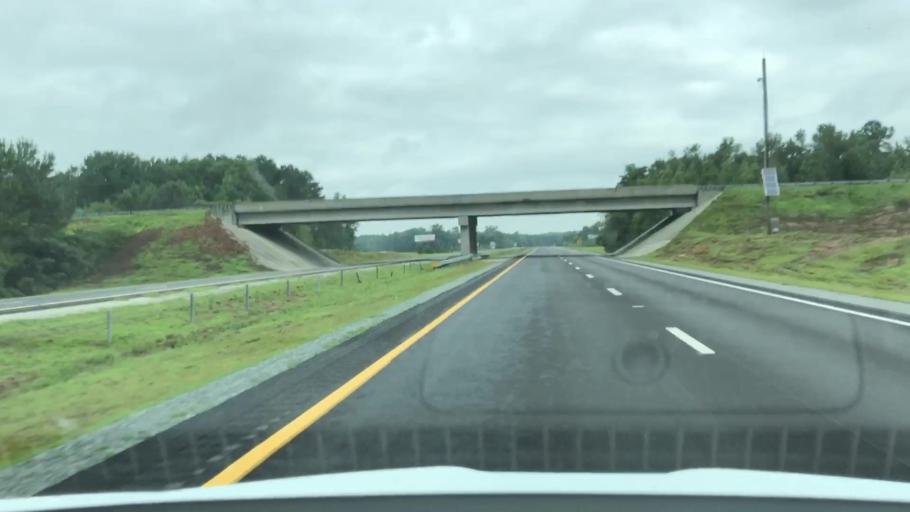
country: US
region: North Carolina
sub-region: Wayne County
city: Fremont
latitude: 35.4944
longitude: -77.9958
